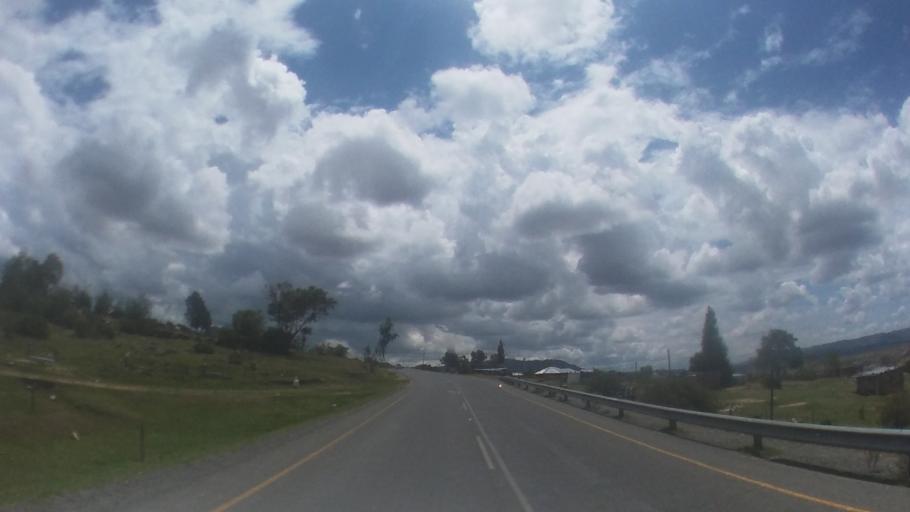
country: LS
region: Maseru
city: Maseru
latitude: -29.4099
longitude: 27.4710
